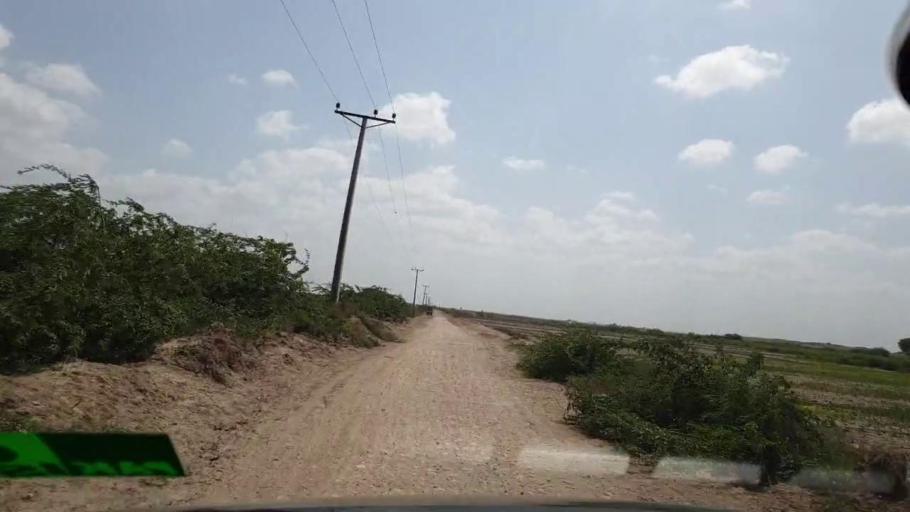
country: PK
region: Sindh
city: Kadhan
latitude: 24.6099
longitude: 69.1852
